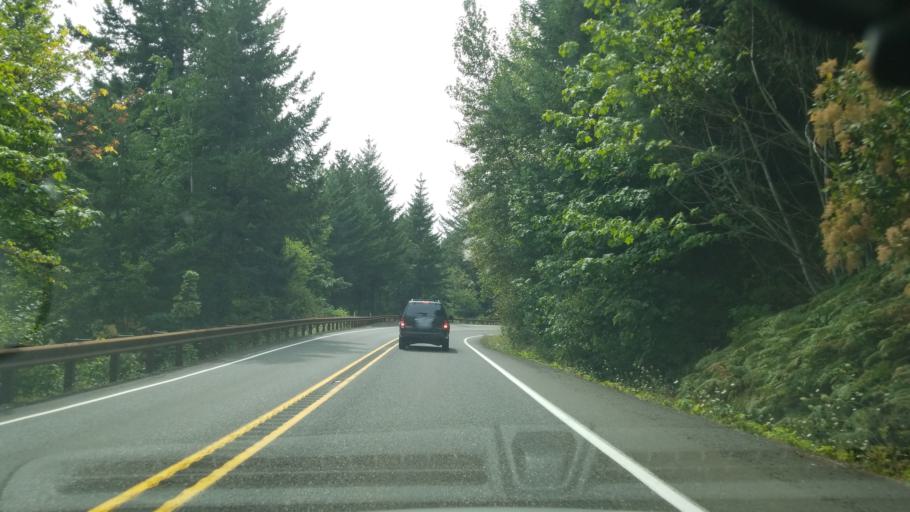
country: US
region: Washington
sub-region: Clark County
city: Washougal
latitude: 45.5601
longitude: -122.2397
